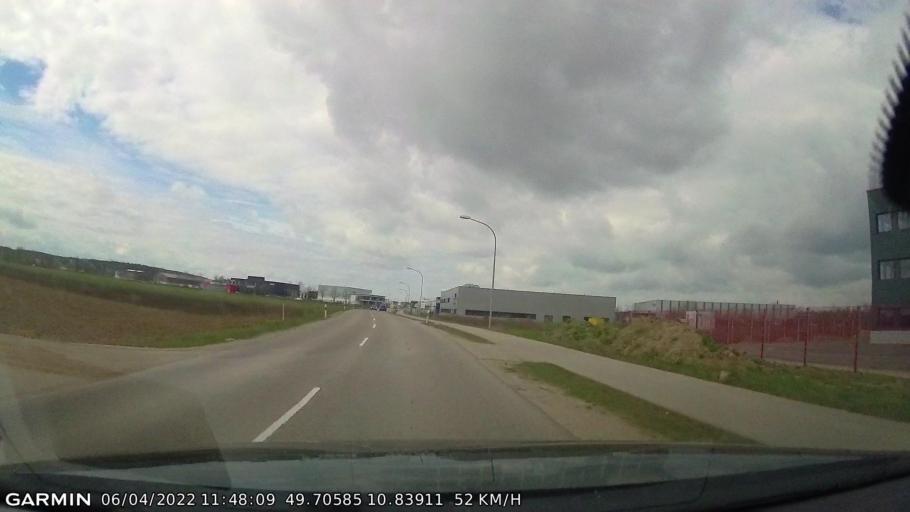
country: DE
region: Bavaria
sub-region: Regierungsbezirk Mittelfranken
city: Gremsdorf
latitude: 49.7058
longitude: 10.8390
